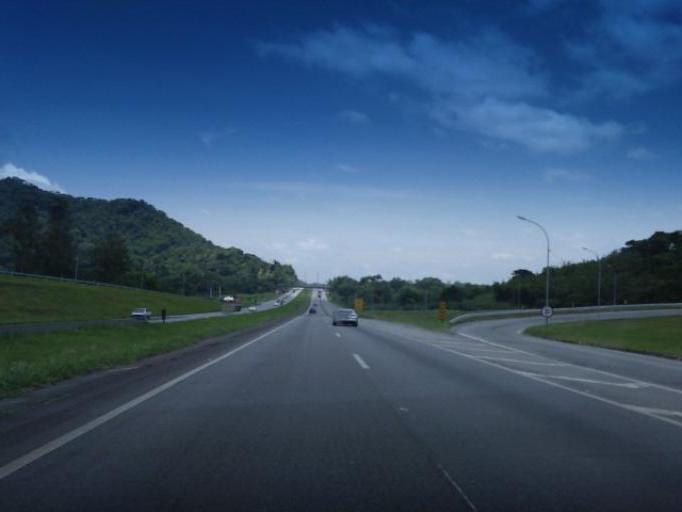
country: BR
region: Sao Paulo
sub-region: Miracatu
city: Miracatu
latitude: -24.3132
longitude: -47.5181
